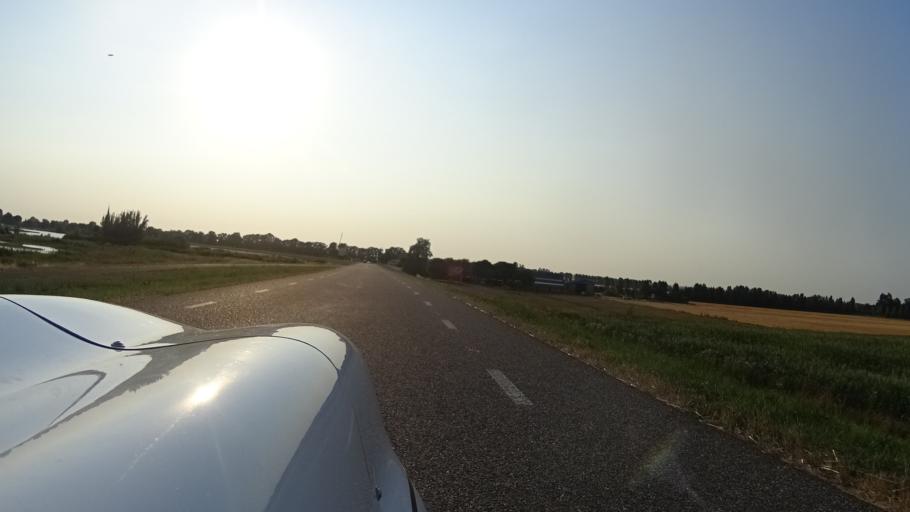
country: NL
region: Gelderland
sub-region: Gemeente Wijchen
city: Bergharen
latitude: 51.8229
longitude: 5.6458
